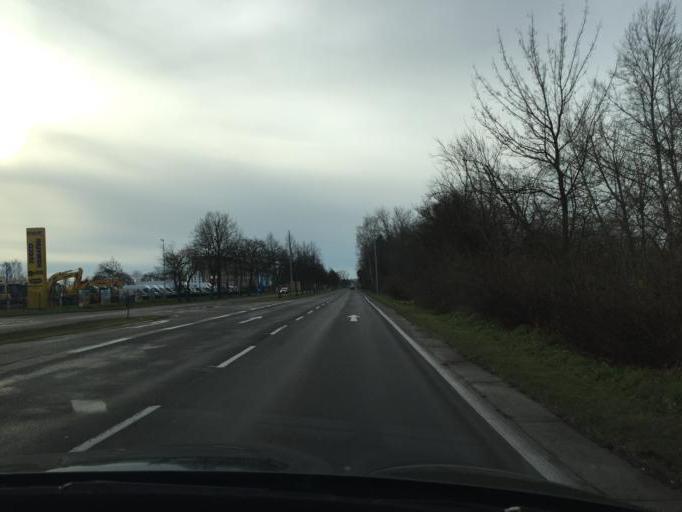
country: DE
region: Brandenburg
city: Cottbus
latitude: 51.7777
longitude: 14.3657
